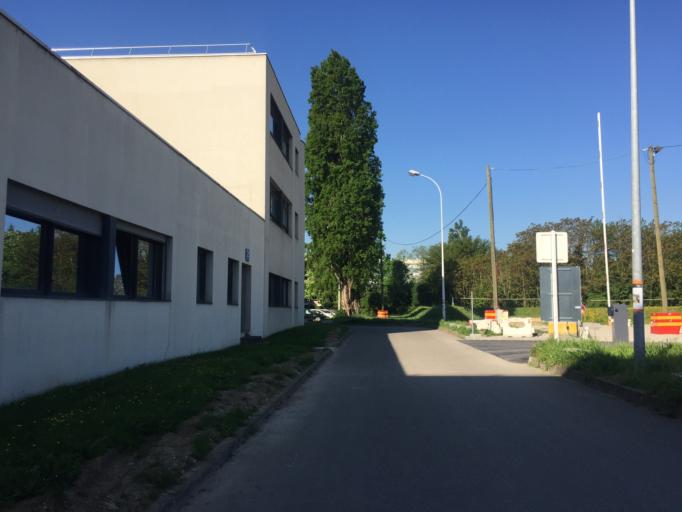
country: FR
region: Rhone-Alpes
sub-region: Departement du Rhone
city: Villeurbanne
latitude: 45.7849
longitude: 4.8824
